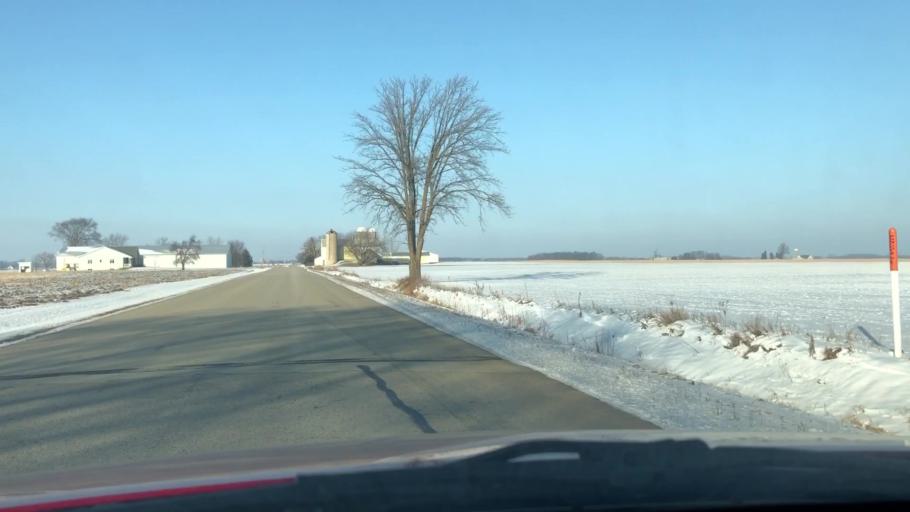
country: US
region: Wisconsin
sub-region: Outagamie County
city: Seymour
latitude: 44.4874
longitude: -88.3090
